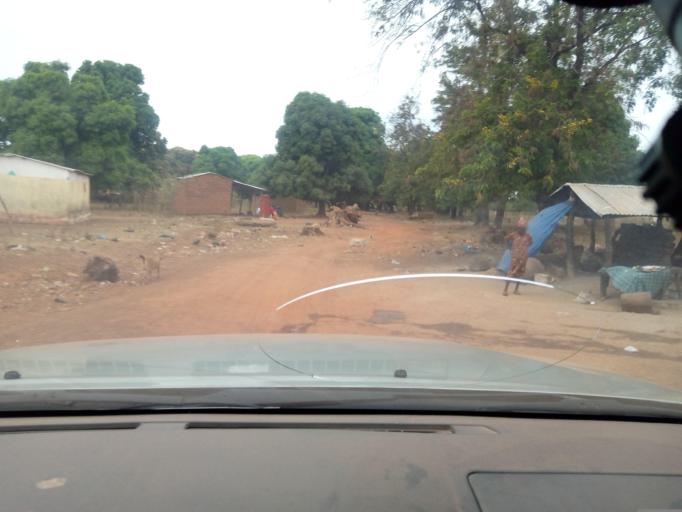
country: ML
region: Sikasso
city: Sikasso
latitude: 10.9702
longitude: -5.6919
